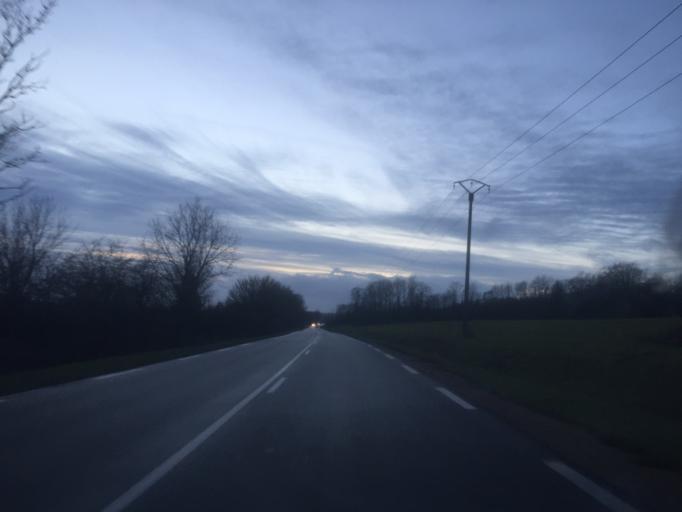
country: FR
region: Franche-Comte
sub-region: Departement du Jura
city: Orchamps
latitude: 47.1458
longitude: 5.6231
